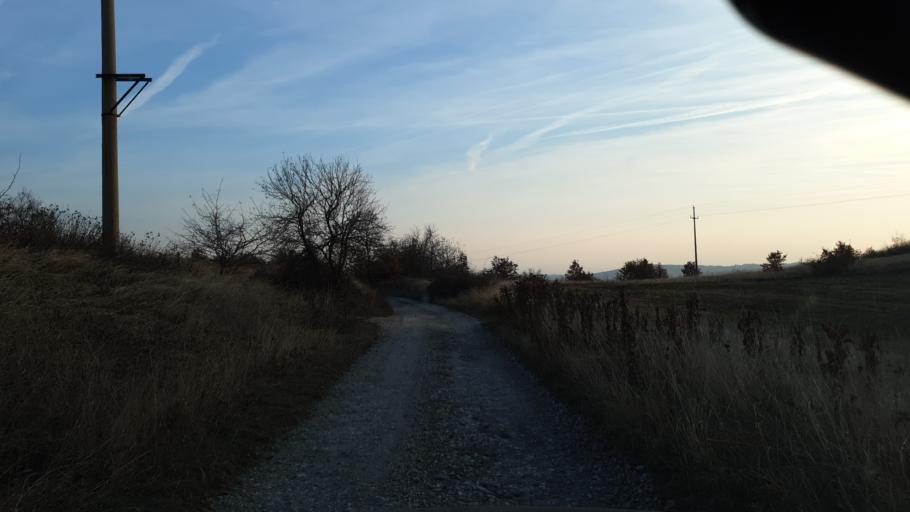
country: RS
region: Central Serbia
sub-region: Borski Okrug
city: Bor
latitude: 44.0646
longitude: 22.0796
